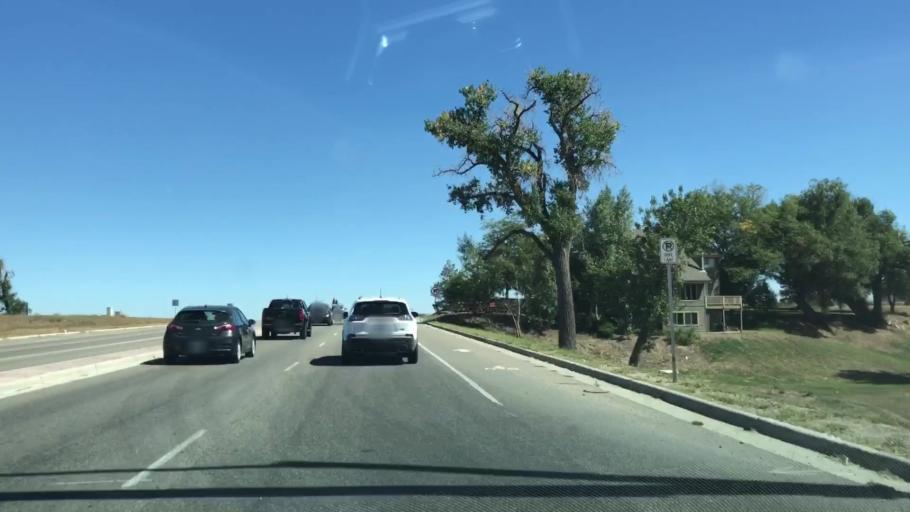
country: US
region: Colorado
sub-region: Weld County
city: Windsor
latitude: 40.5229
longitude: -104.9819
